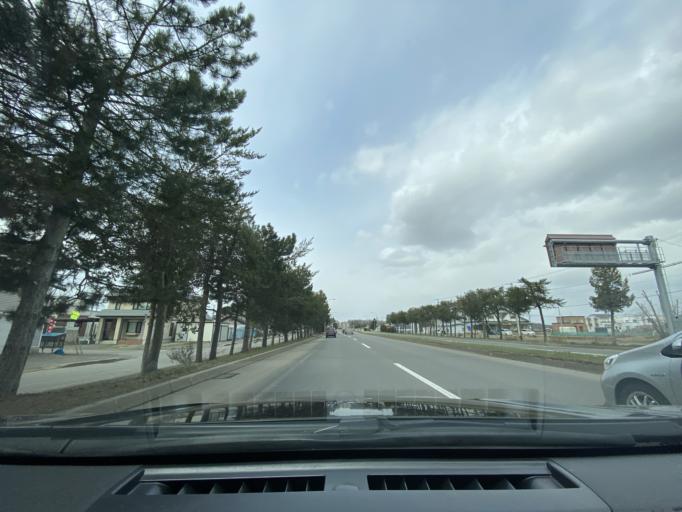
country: JP
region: Hokkaido
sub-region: Asahikawa-shi
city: Asahikawa
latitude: 43.8174
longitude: 142.3988
